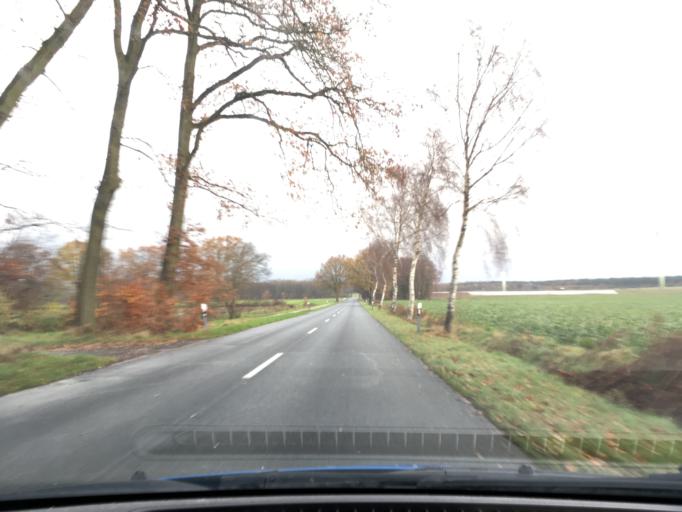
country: DE
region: Lower Saxony
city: Embsen
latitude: 53.1821
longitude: 10.3476
